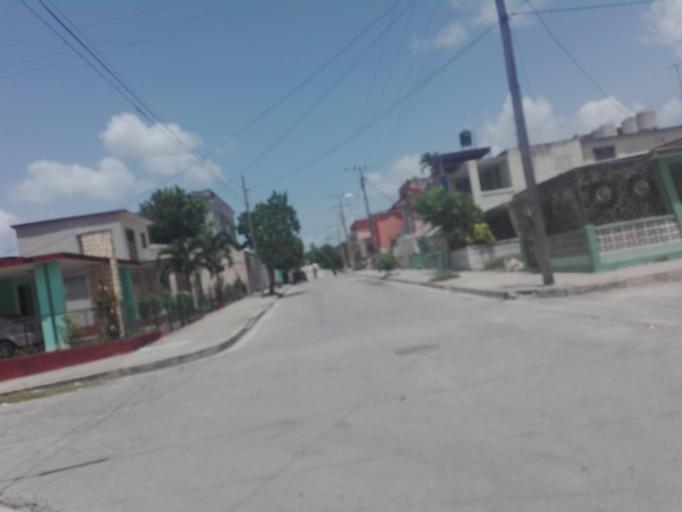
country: CU
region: Cienfuegos
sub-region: Municipio de Cienfuegos
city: Cienfuegos
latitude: 22.1476
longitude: -80.4394
